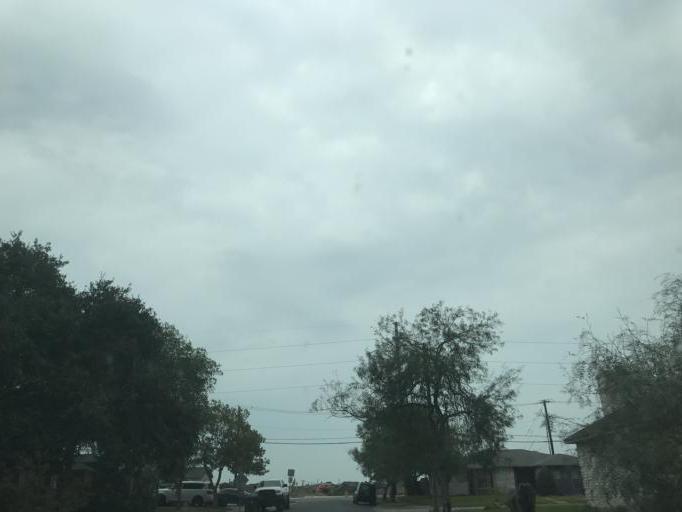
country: US
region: Texas
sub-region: Nueces County
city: Corpus Christi
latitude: 27.6750
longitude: -97.3480
